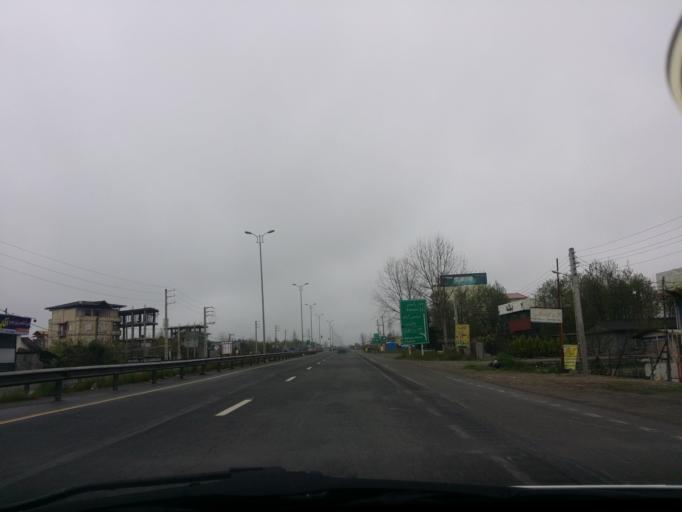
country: IR
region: Mazandaran
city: Tonekabon
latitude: 36.8021
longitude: 50.8839
